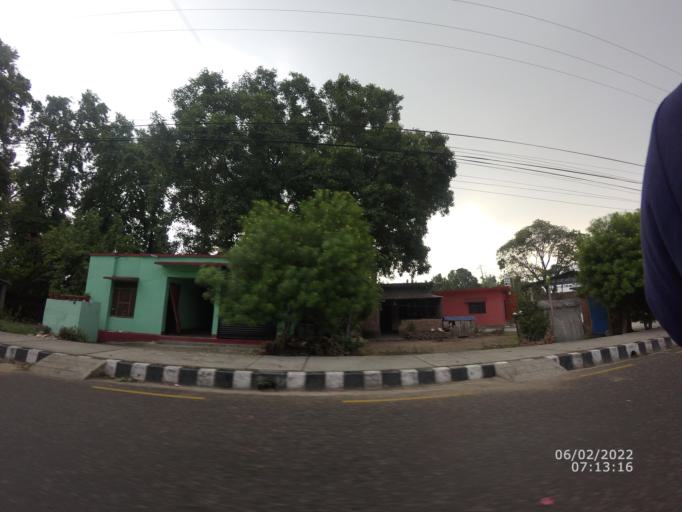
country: NP
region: Western Region
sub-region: Lumbini Zone
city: Bhairahawa
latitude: 27.4823
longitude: 83.4423
